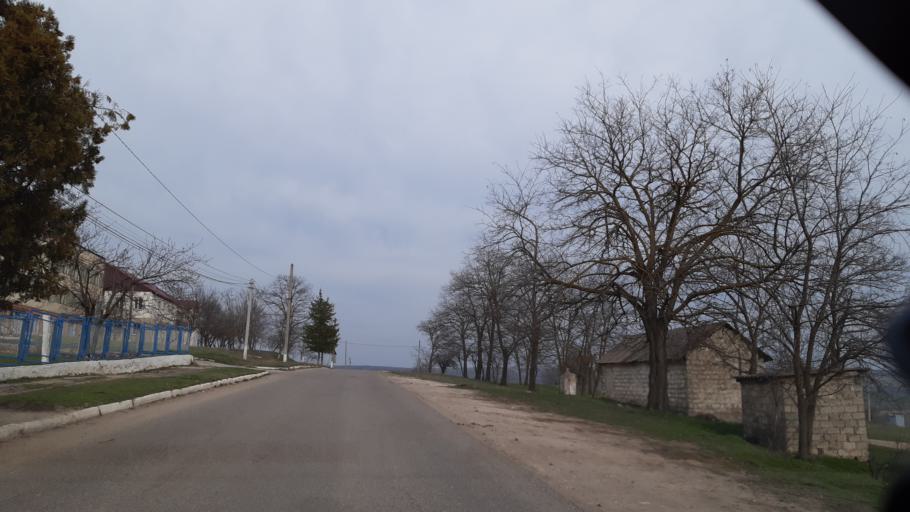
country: MD
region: Soldanesti
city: Soldanesti
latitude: 47.6842
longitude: 28.7699
